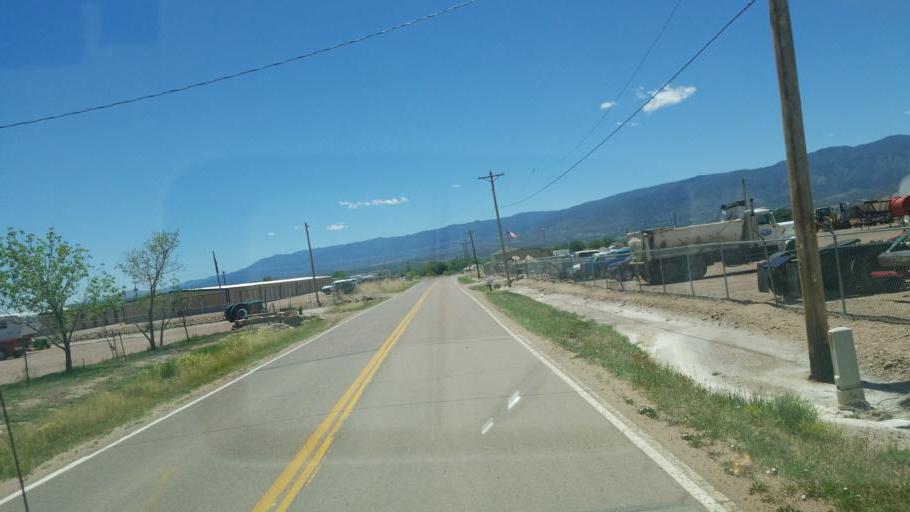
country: US
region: Colorado
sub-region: Fremont County
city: Canon City
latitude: 38.4738
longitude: -105.2226
